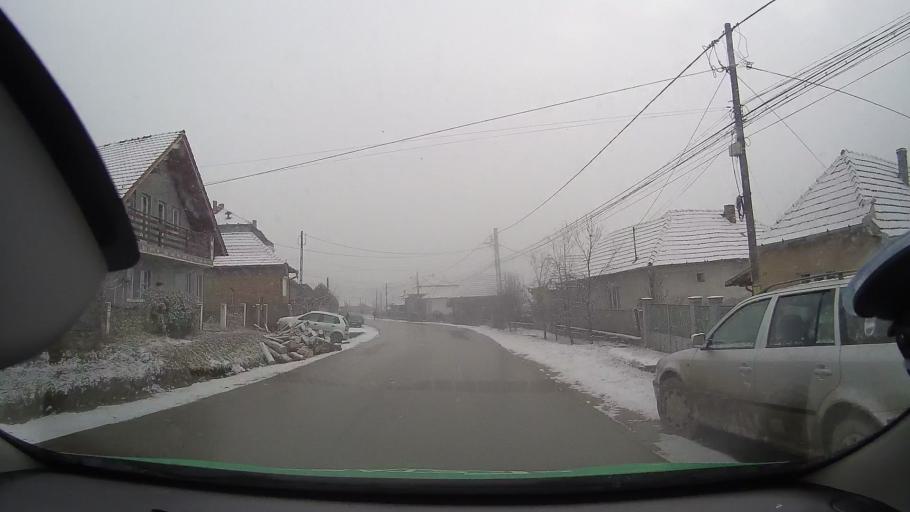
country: RO
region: Alba
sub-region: Comuna Lopadea Noua
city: Lopadea Noua
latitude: 46.2913
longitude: 23.8209
